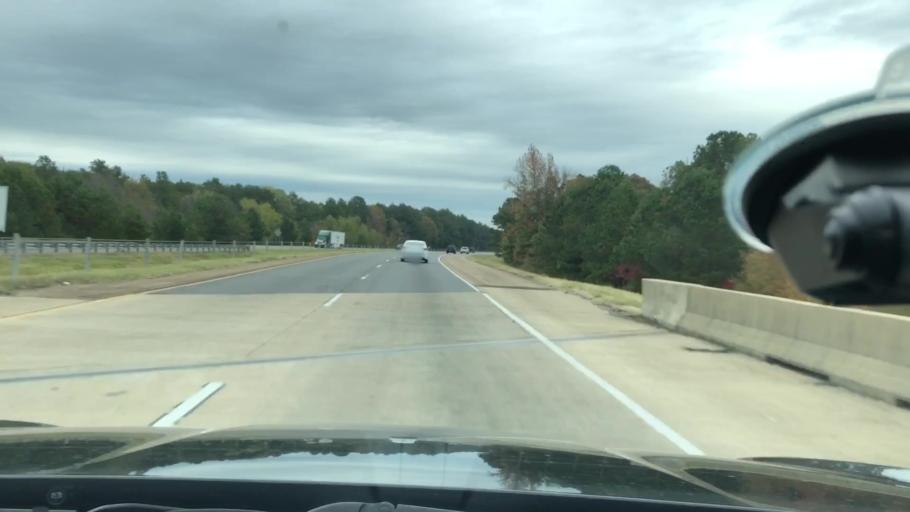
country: US
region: Arkansas
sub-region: Clark County
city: Gurdon
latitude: 33.9513
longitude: -93.2335
